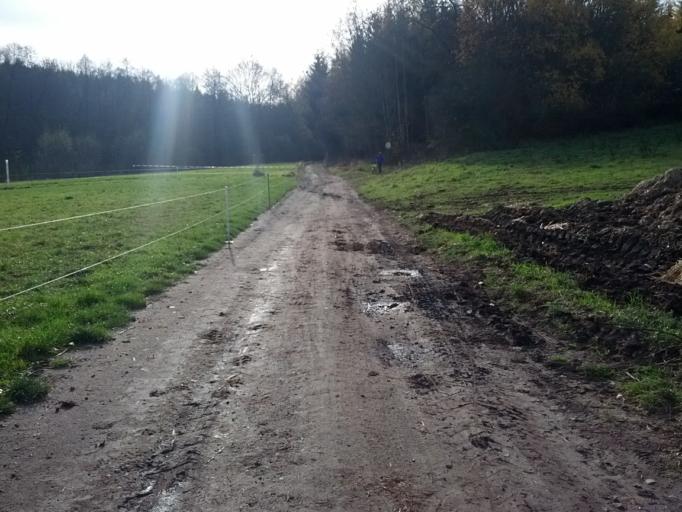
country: DE
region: Thuringia
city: Eisenach
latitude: 50.9582
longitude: 10.3580
